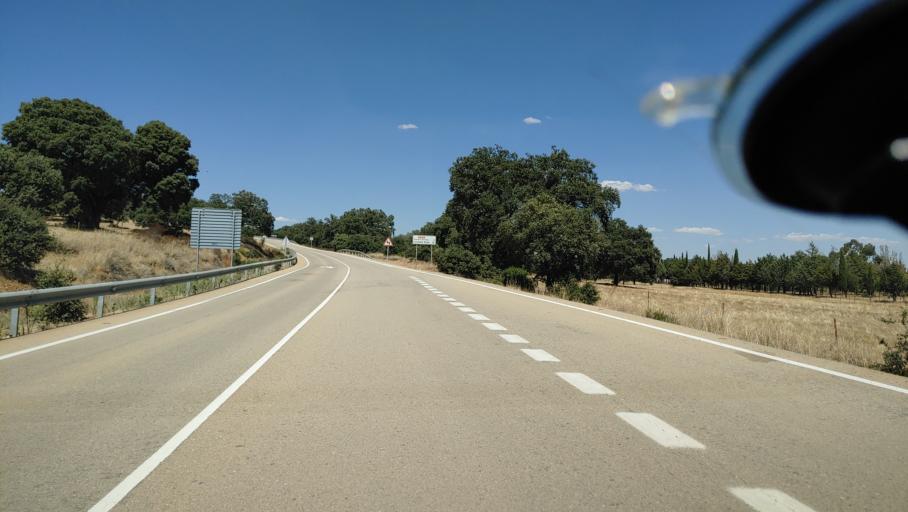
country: ES
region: Castille-La Mancha
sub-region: Provincia de Ciudad Real
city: Saceruela
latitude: 38.9547
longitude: -4.6105
